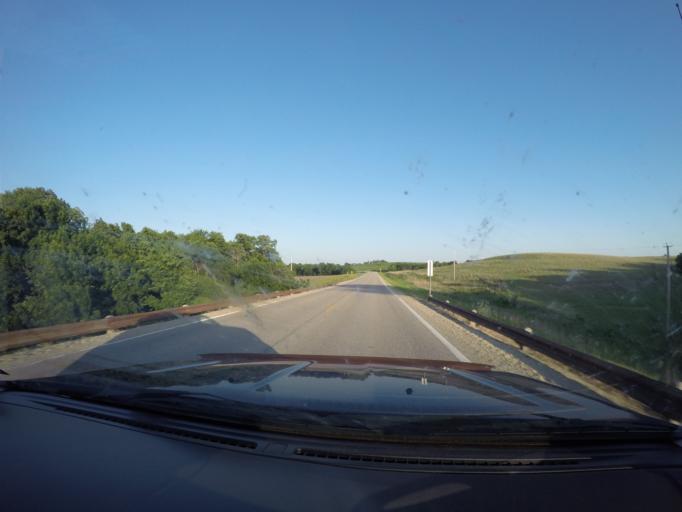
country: US
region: Kansas
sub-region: Marshall County
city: Blue Rapids
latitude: 39.6936
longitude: -96.7889
